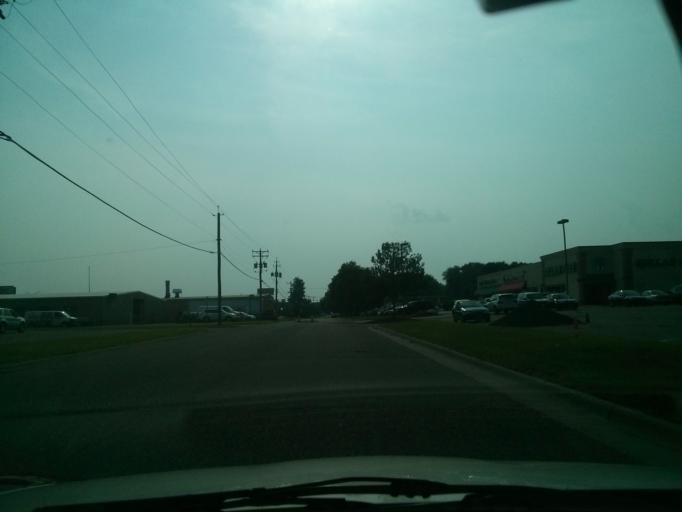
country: US
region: Wisconsin
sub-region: Saint Croix County
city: Hudson
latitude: 44.9642
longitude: -92.7332
